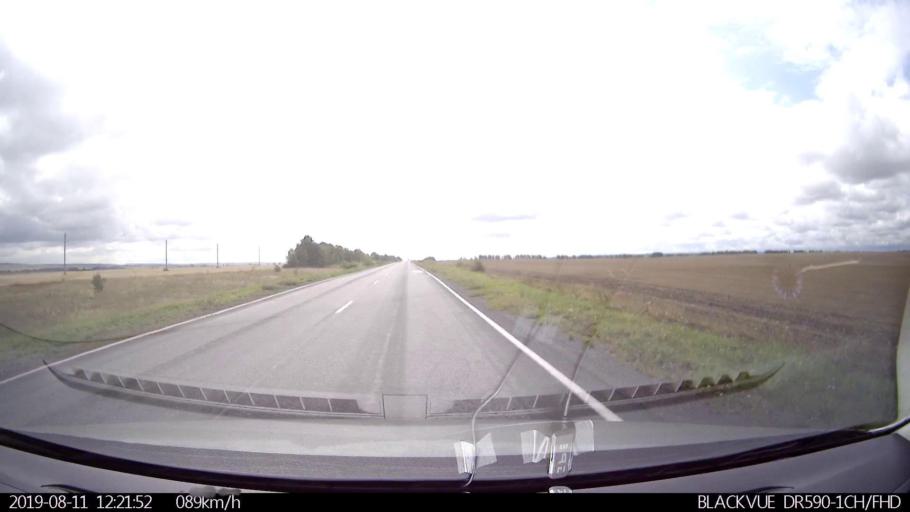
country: RU
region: Ulyanovsk
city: Ignatovka
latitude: 53.9156
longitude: 47.9563
